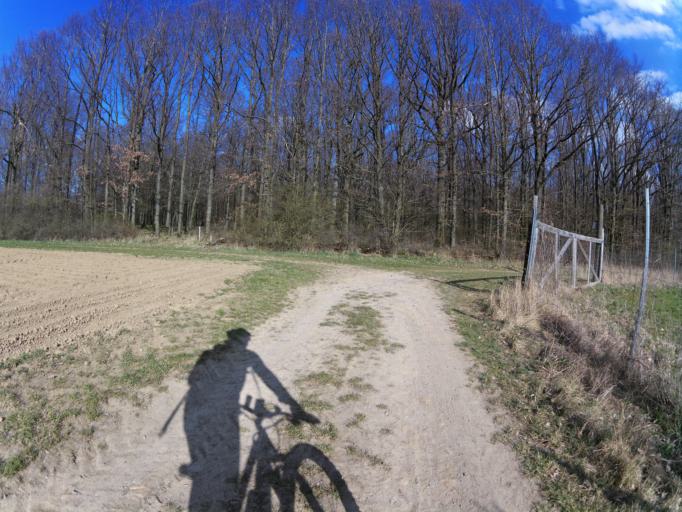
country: DE
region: Bavaria
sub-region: Regierungsbezirk Unterfranken
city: Nordheim
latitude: 49.8444
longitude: 10.1601
